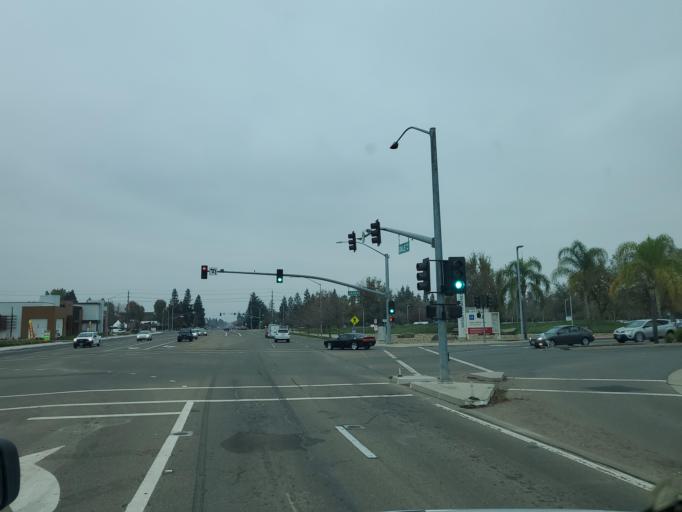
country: US
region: California
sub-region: Stanislaus County
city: Salida
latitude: 37.7060
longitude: -121.0501
